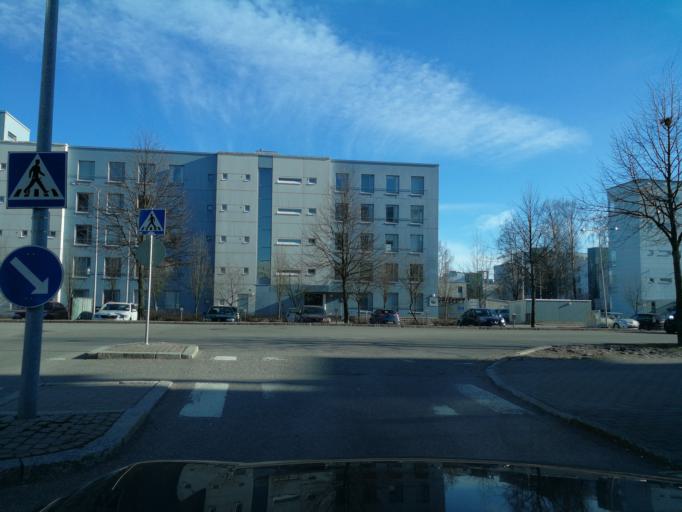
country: FI
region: Uusimaa
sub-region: Helsinki
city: Vantaa
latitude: 60.2058
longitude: 25.1375
